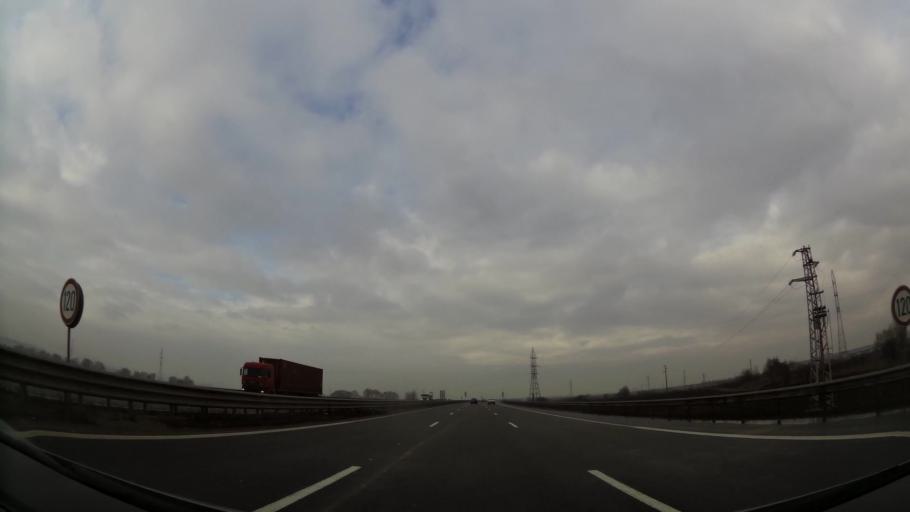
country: BG
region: Sofia-Capital
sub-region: Stolichna Obshtina
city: Sofia
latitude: 42.7599
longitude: 23.3140
